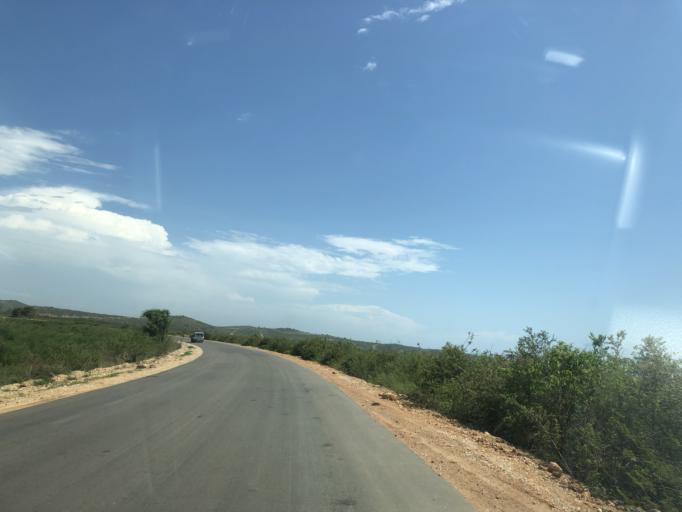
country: AO
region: Cuanza Sul
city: Sumbe
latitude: -10.8788
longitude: 13.8393
